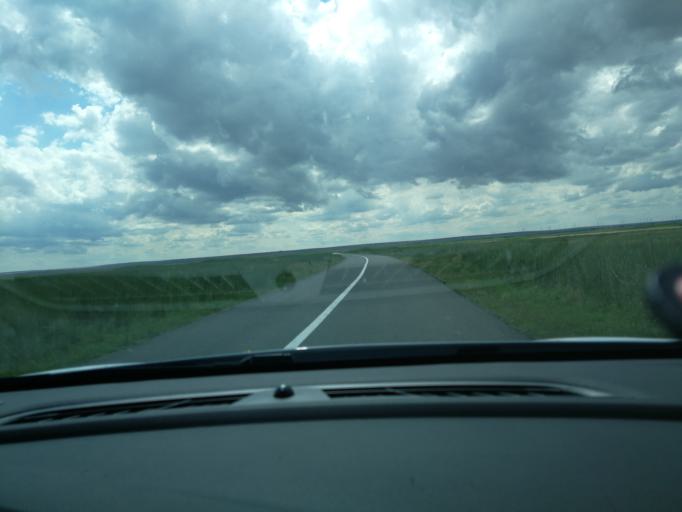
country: RO
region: Constanta
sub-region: Comuna Istria
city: Istria
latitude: 44.5361
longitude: 28.7366
